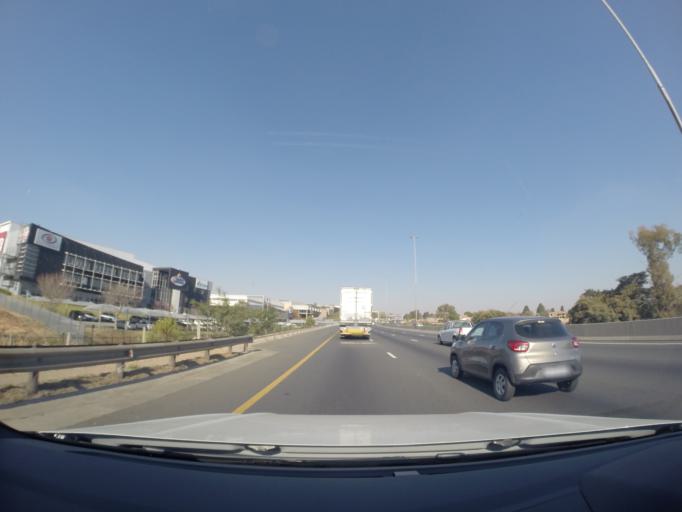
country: ZA
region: Gauteng
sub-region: City of Johannesburg Metropolitan Municipality
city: Modderfontein
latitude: -26.0844
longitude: 28.1189
